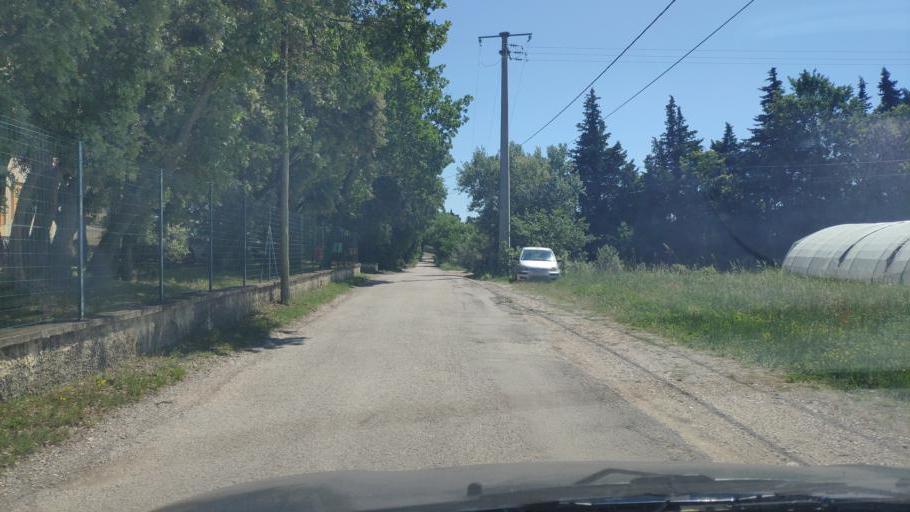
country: FR
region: Provence-Alpes-Cote d'Azur
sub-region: Departement du Vaucluse
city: Carpentras
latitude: 44.0838
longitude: 5.0566
